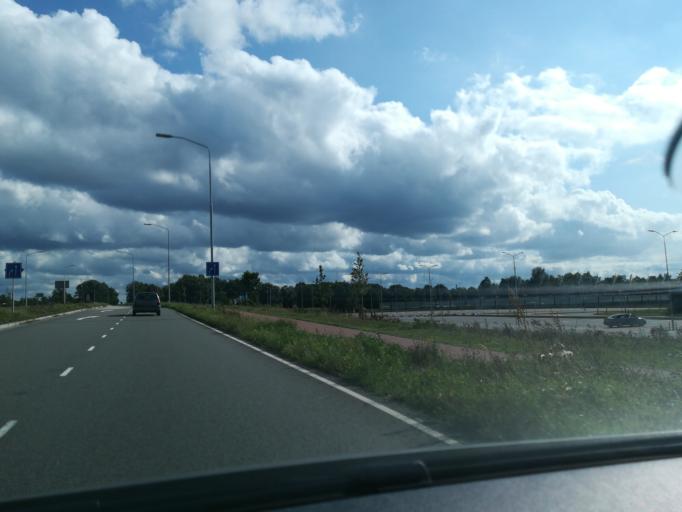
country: NL
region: North Brabant
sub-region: Gemeente Veldhoven
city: Veldhoven
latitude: 51.4061
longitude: 5.4226
